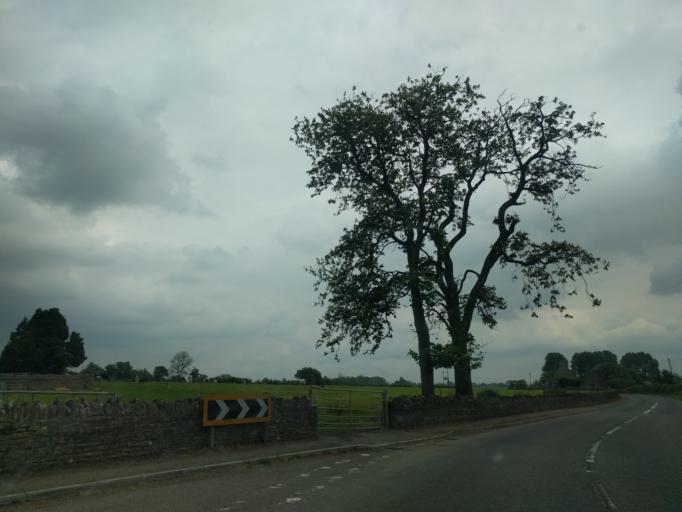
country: GB
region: England
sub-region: Somerset
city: Ilchester
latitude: 51.0722
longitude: -2.6789
